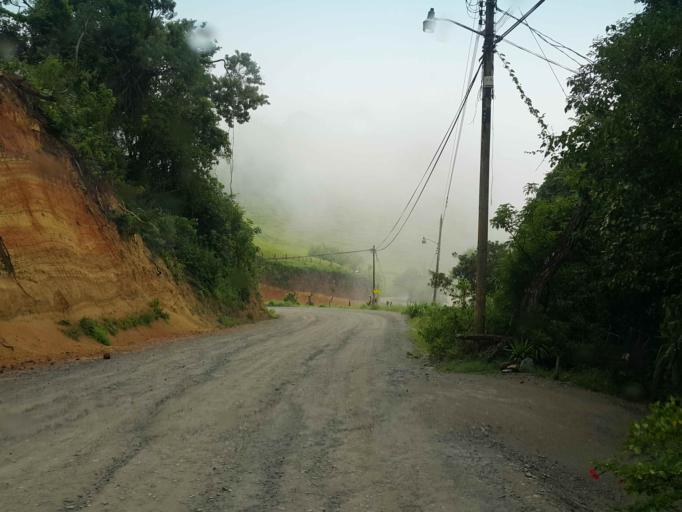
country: CR
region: Guanacaste
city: Juntas
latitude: 10.2852
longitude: -84.8356
